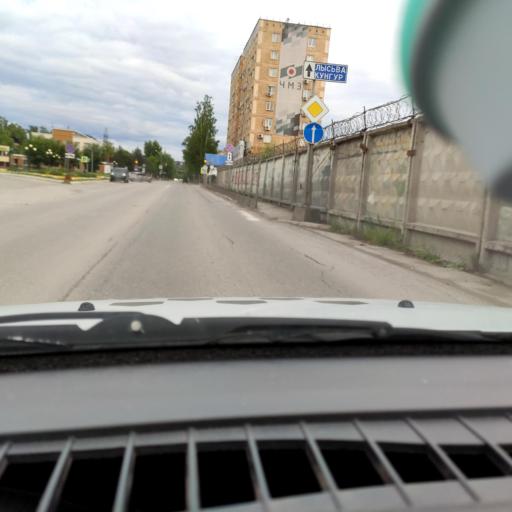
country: RU
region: Perm
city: Chusovoy
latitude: 58.2960
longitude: 57.8124
